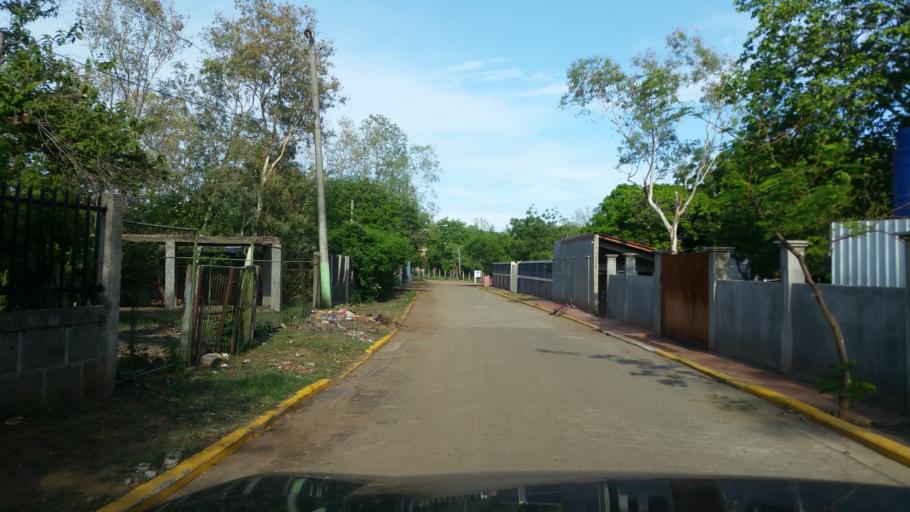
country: NI
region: Managua
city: Masachapa
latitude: 11.7766
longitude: -86.5151
